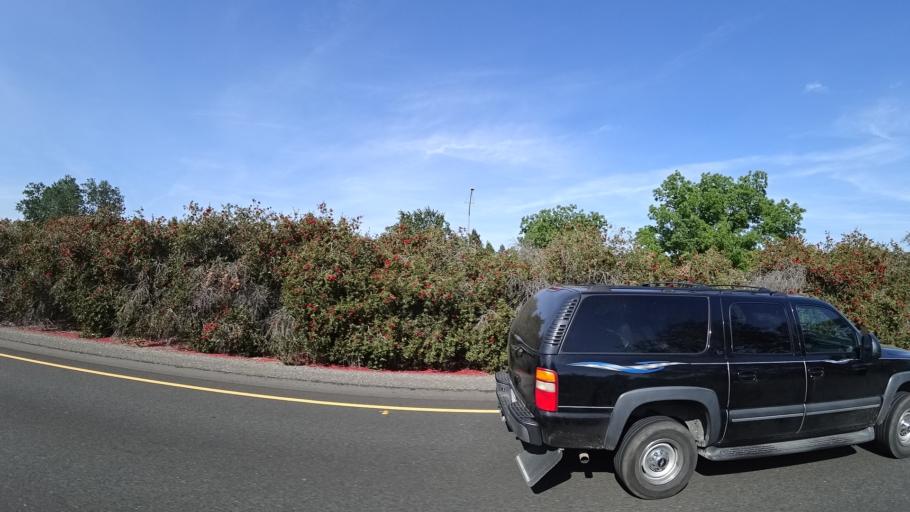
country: US
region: California
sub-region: Butte County
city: Chico
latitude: 39.7623
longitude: -121.8585
